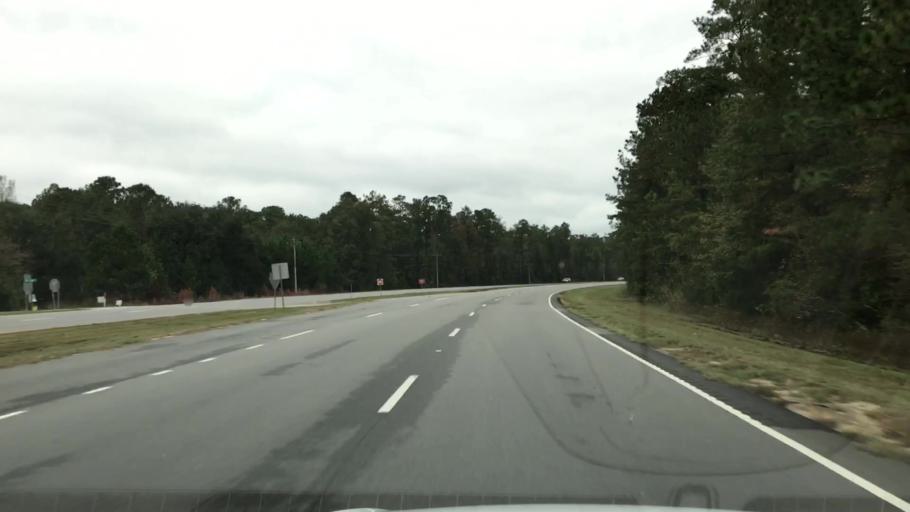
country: US
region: South Carolina
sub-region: Georgetown County
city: Georgetown
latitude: 33.2491
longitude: -79.3750
